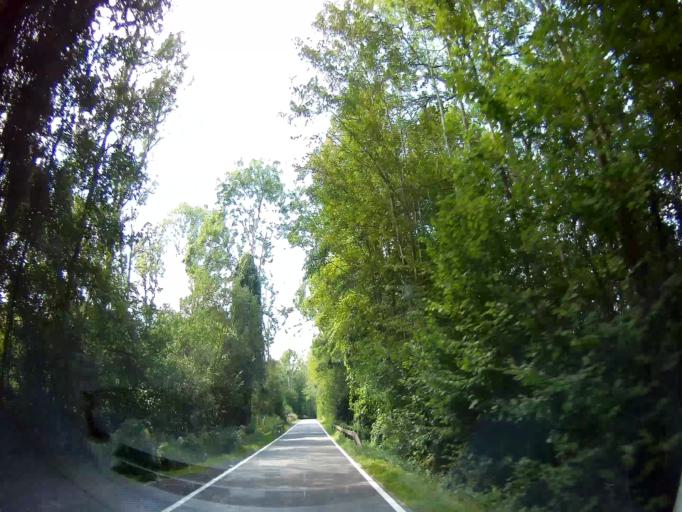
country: BE
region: Wallonia
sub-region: Province de Namur
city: Yvoir
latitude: 50.3525
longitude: 4.9283
